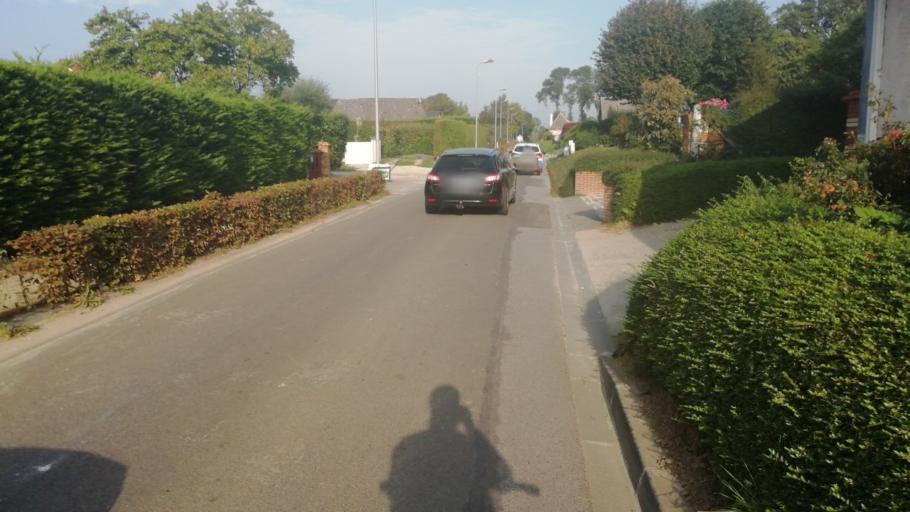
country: FR
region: Haute-Normandie
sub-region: Departement de la Seine-Maritime
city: Saint-Romain-de-Colbosc
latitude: 49.4976
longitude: 0.3679
